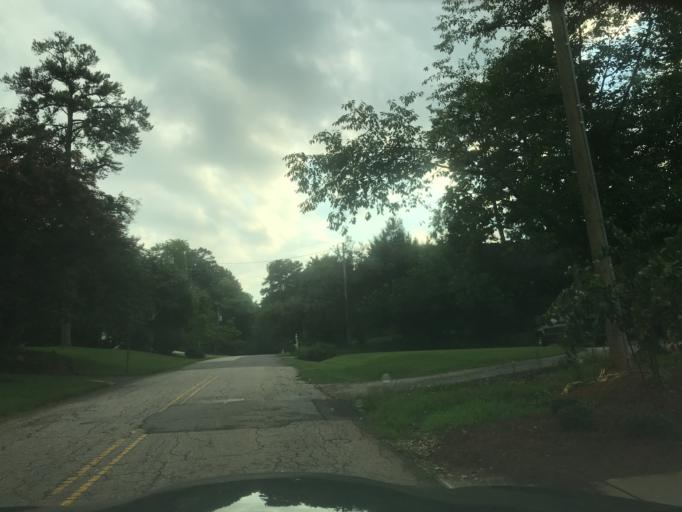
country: US
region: North Carolina
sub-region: Wake County
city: West Raleigh
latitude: 35.8335
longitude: -78.6600
